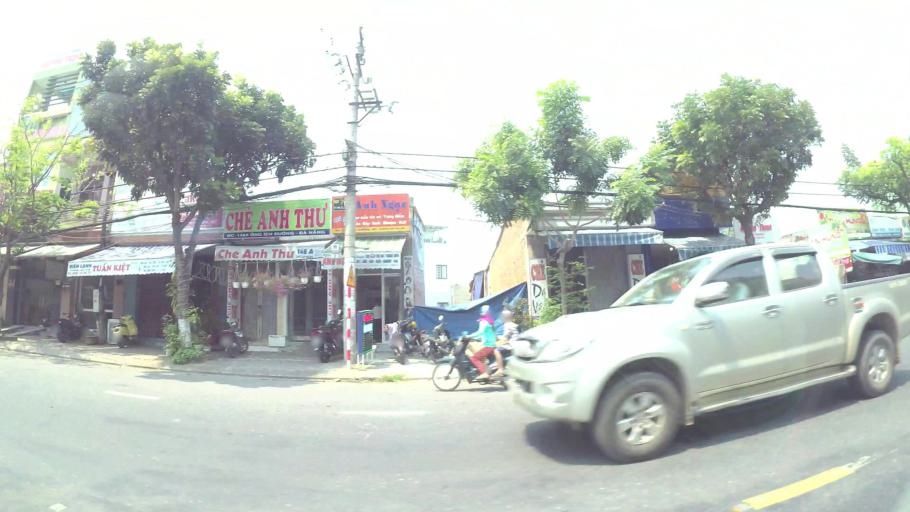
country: VN
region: Da Nang
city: Cam Le
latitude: 16.0133
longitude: 108.2056
